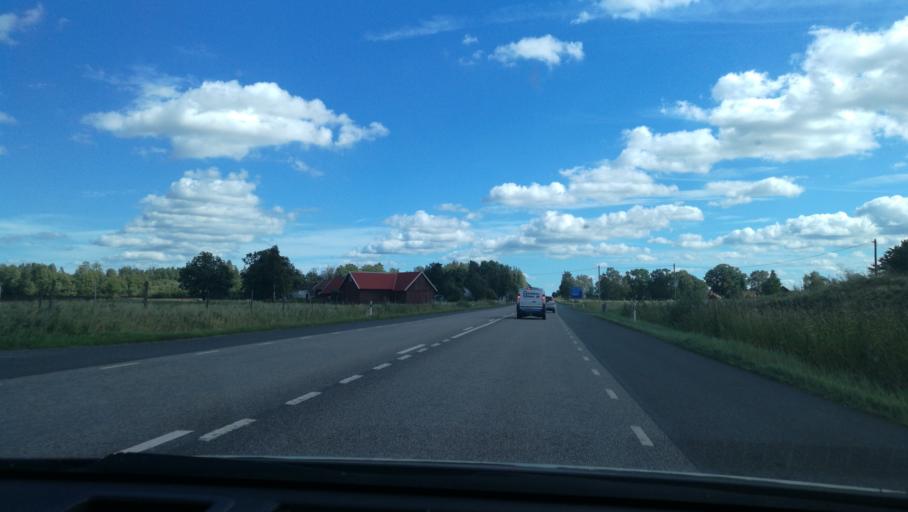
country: SE
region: Vaestra Goetaland
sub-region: Gotene Kommun
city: Kallby
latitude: 58.5116
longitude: 13.3422
